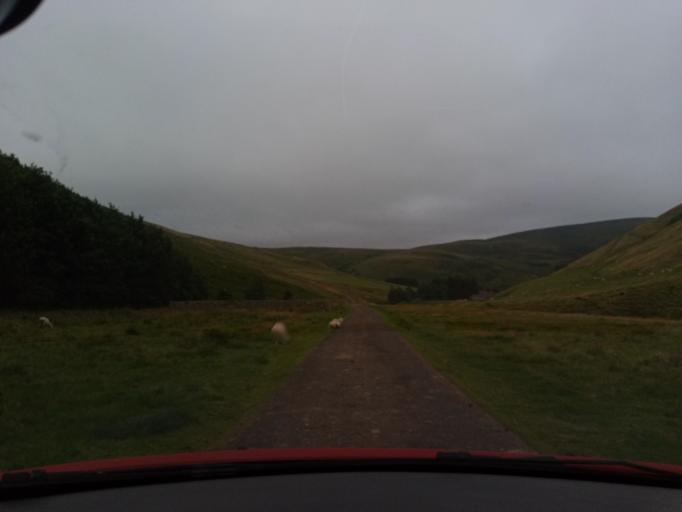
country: GB
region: England
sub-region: Northumberland
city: Rochester
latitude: 55.3950
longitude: -2.2201
